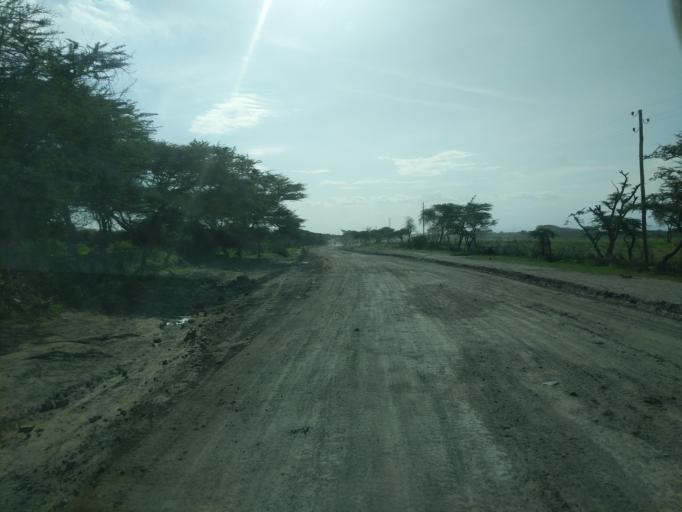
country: ET
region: Oromiya
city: Ziway
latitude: 7.5849
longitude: 38.6811
